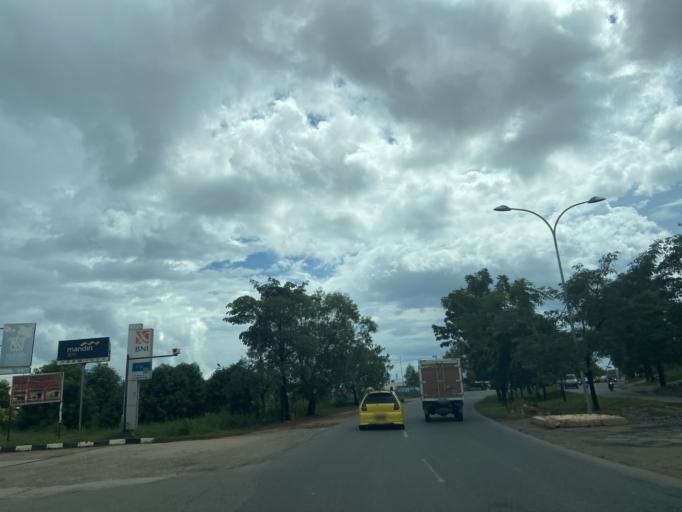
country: SG
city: Singapore
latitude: 1.0403
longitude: 103.9862
